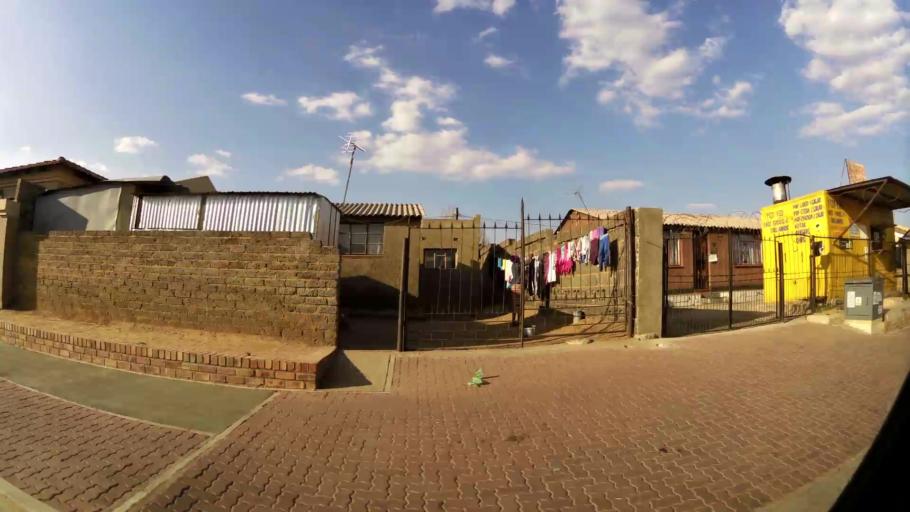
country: ZA
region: Gauteng
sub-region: City of Johannesburg Metropolitan Municipality
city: Soweto
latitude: -26.2262
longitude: 27.8934
